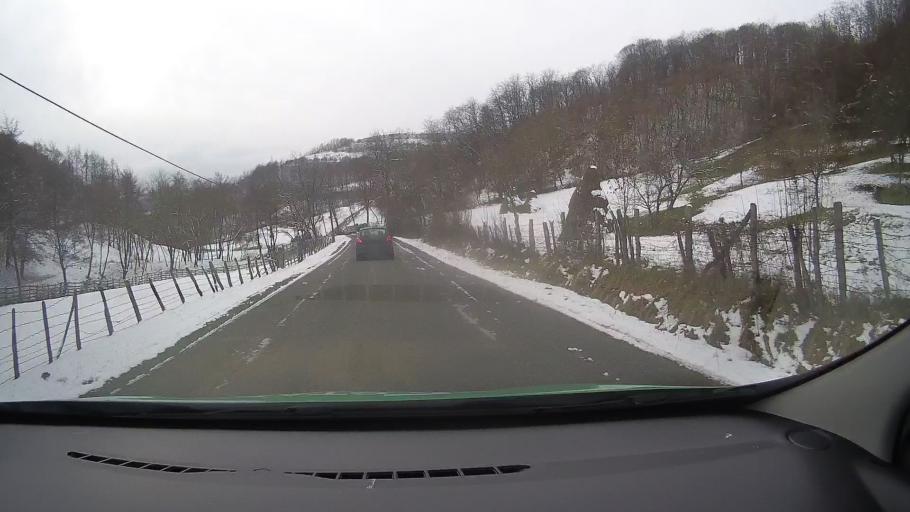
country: RO
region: Alba
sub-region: Comuna Almasu Mare
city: Almasu Mare
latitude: 46.0772
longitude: 23.1100
